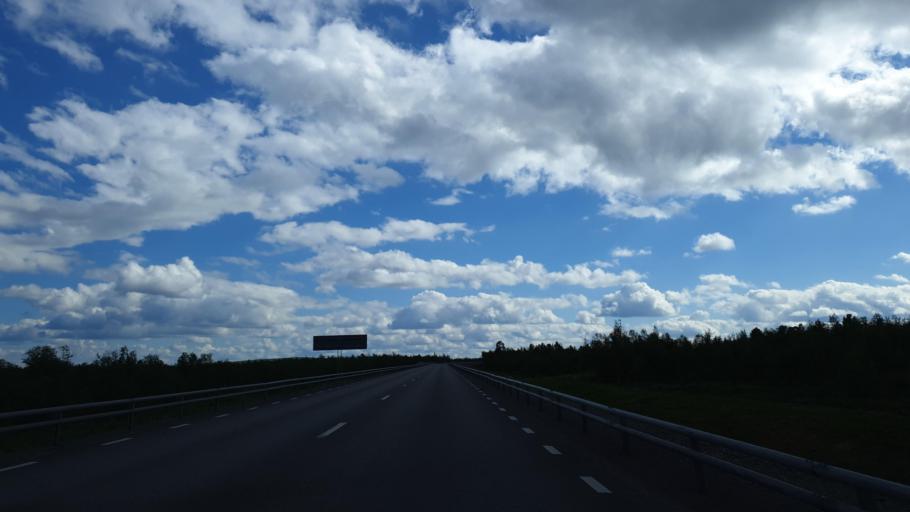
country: SE
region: Norrbotten
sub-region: Kiruna Kommun
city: Kiruna
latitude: 67.8413
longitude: 20.3079
